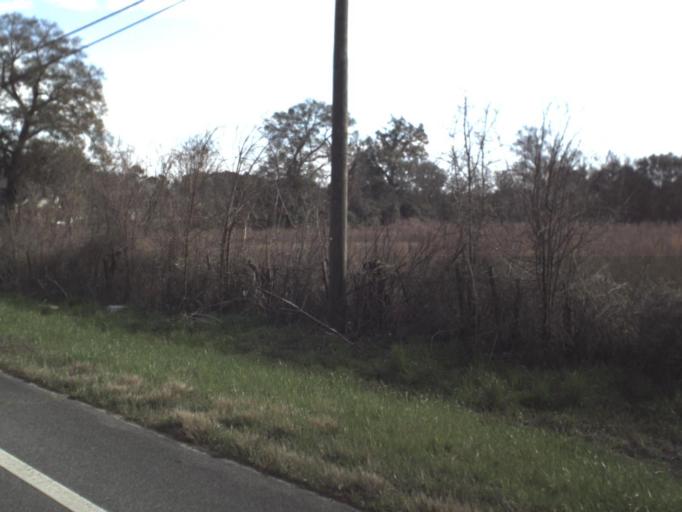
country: US
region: Florida
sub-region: Jackson County
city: Marianna
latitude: 30.8222
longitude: -85.1705
